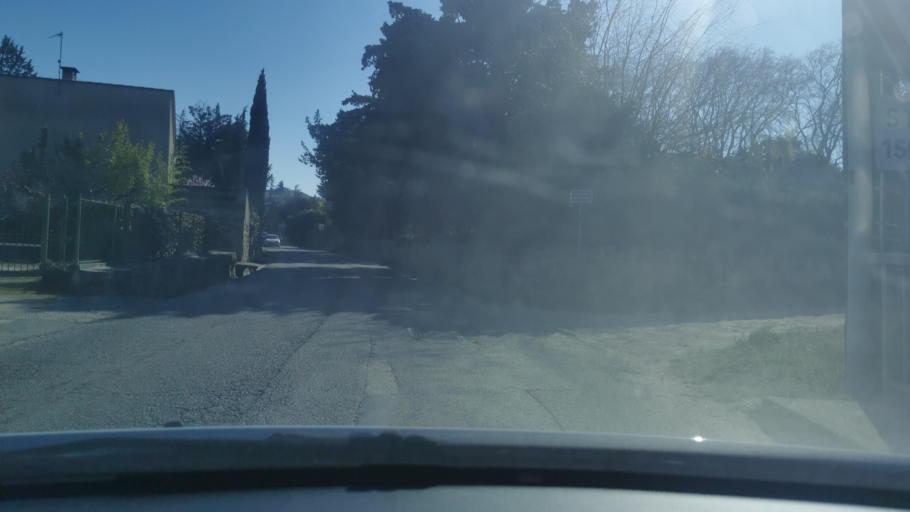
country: FR
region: Languedoc-Roussillon
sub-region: Departement du Gard
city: Saint-Quentin-la-Poterie
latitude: 44.0477
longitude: 4.4360
